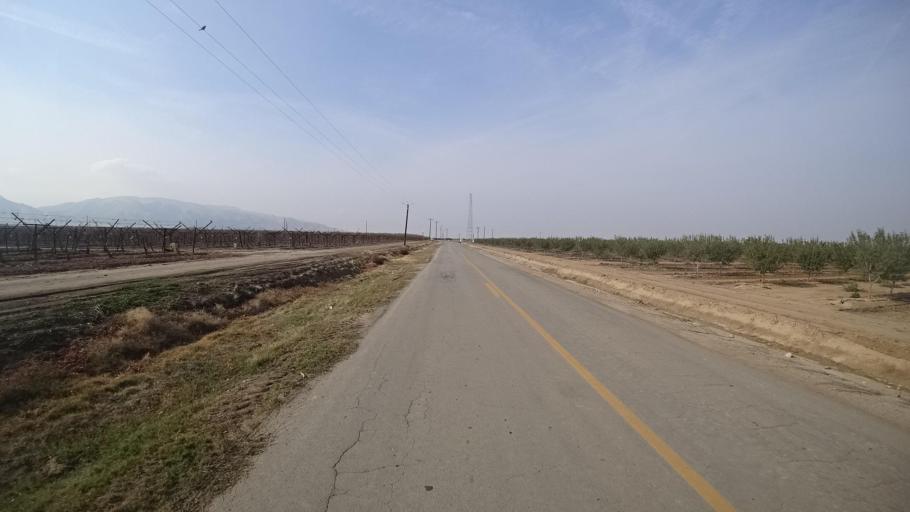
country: US
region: California
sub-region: Kern County
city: Weedpatch
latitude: 35.0337
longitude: -118.9554
